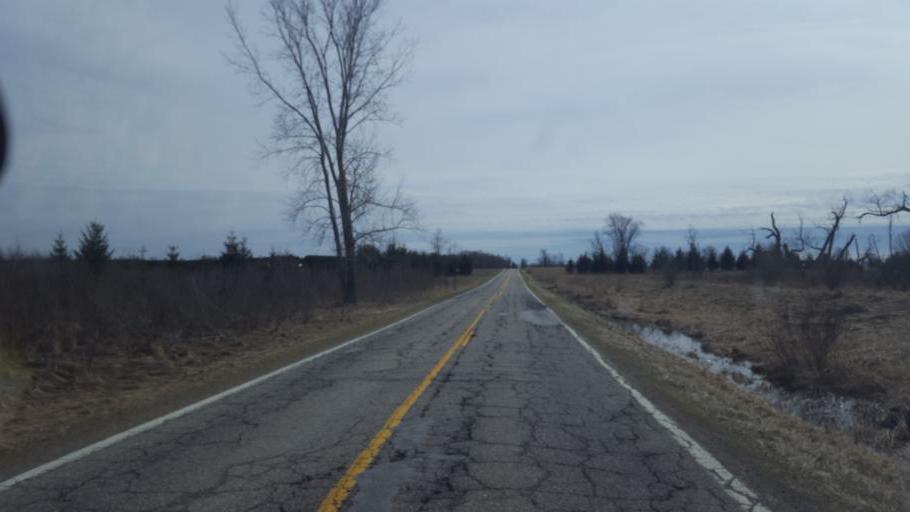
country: US
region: Michigan
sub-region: Isabella County
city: Lake Isabella
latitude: 43.5867
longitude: -85.0265
